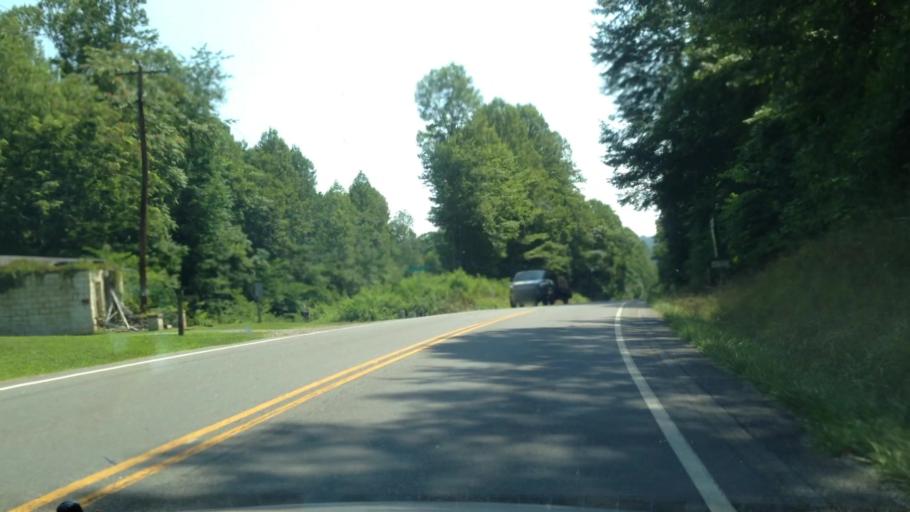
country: US
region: Virginia
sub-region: Patrick County
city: Stuart
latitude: 36.5894
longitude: -80.3284
